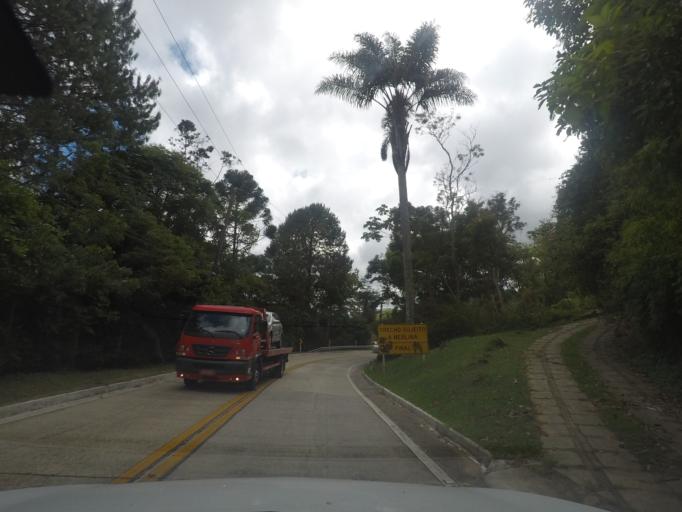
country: BR
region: Rio de Janeiro
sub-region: Teresopolis
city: Teresopolis
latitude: -22.3962
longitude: -42.9934
